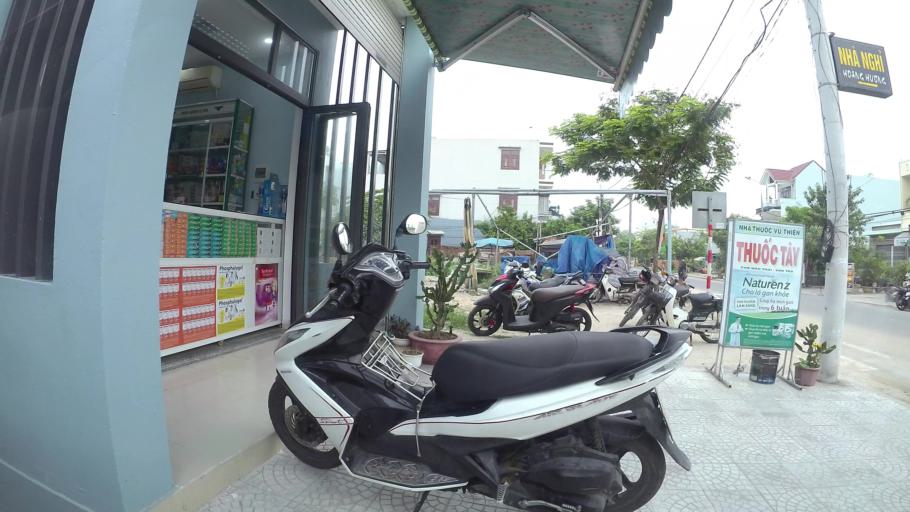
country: VN
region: Da Nang
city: Son Tra
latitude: 16.0863
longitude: 108.2429
